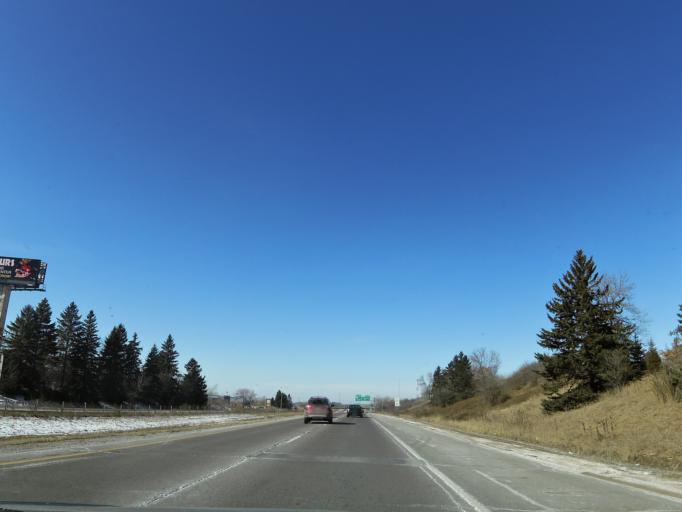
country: US
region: Minnesota
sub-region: Ramsey County
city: Arden Hills
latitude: 45.0580
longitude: -93.1389
